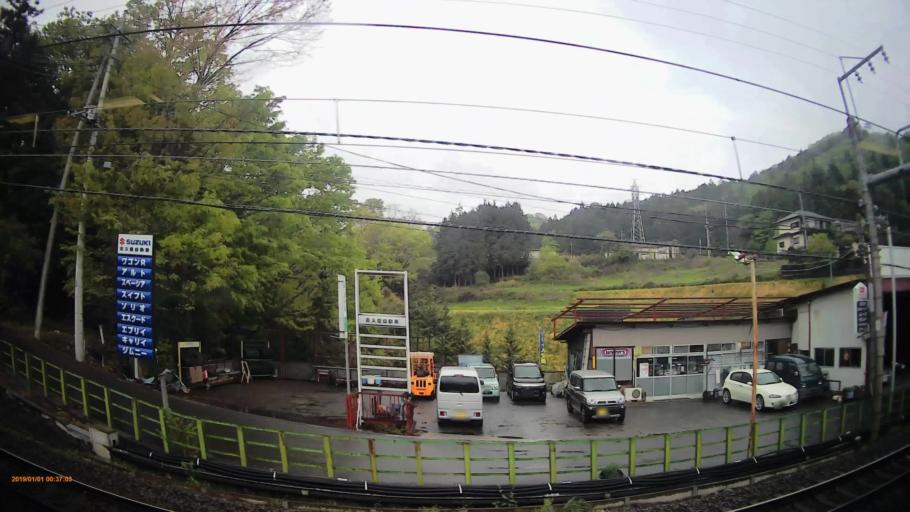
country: JP
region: Yamanashi
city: Otsuki
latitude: 35.6076
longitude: 139.0132
